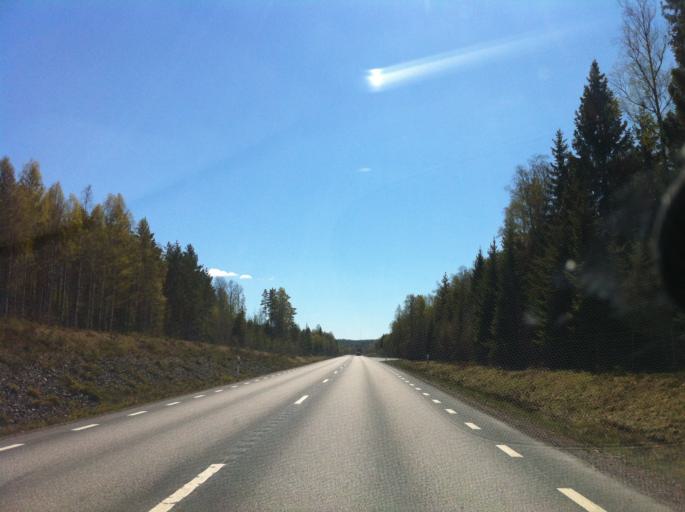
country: SE
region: Kalmar
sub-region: Vimmerby Kommun
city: Vimmerby
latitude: 57.6284
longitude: 15.8392
